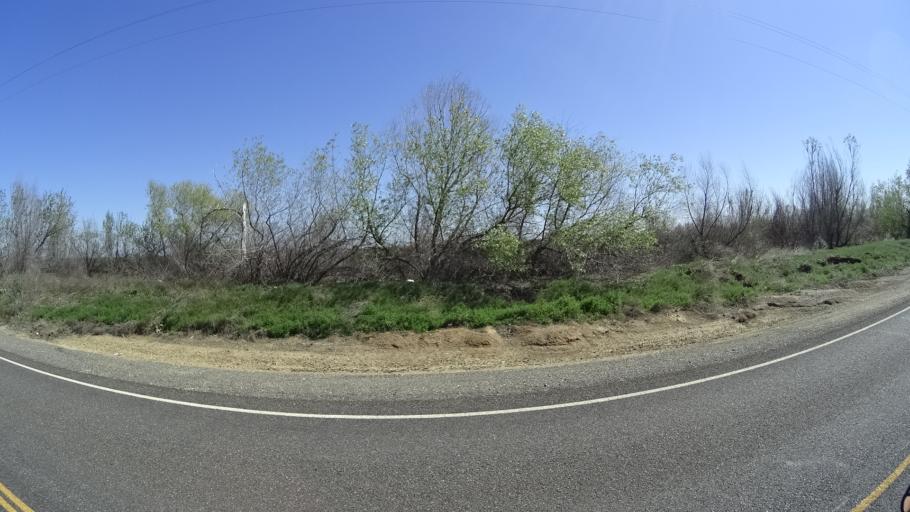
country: US
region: California
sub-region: Glenn County
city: Willows
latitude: 39.6131
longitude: -122.2500
